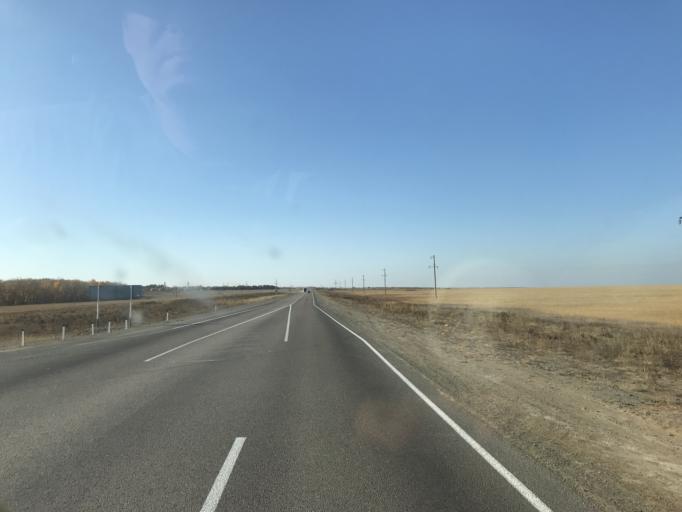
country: KZ
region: Pavlodar
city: Koktobe
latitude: 51.4966
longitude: 77.7180
